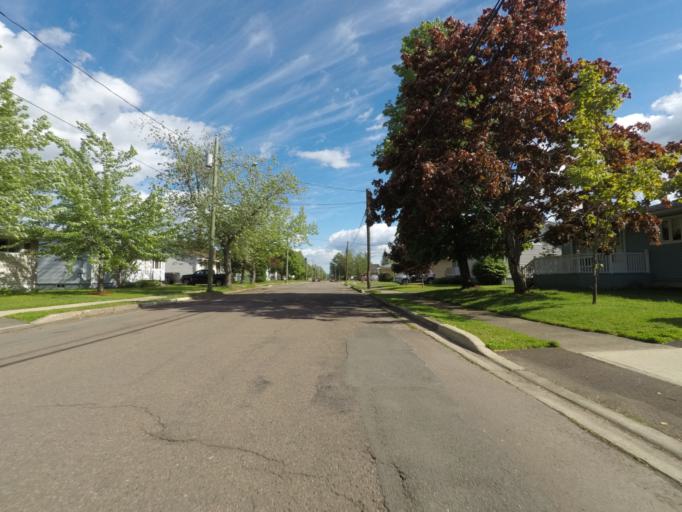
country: CA
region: New Brunswick
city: Moncton
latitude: 46.1024
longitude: -64.8273
